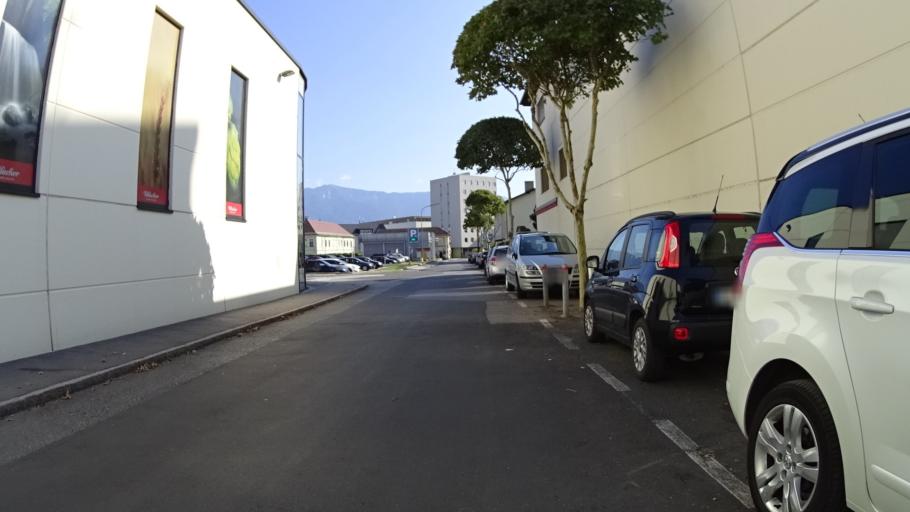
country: AT
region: Carinthia
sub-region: Villach Stadt
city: Villach
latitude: 46.6165
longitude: 13.8516
